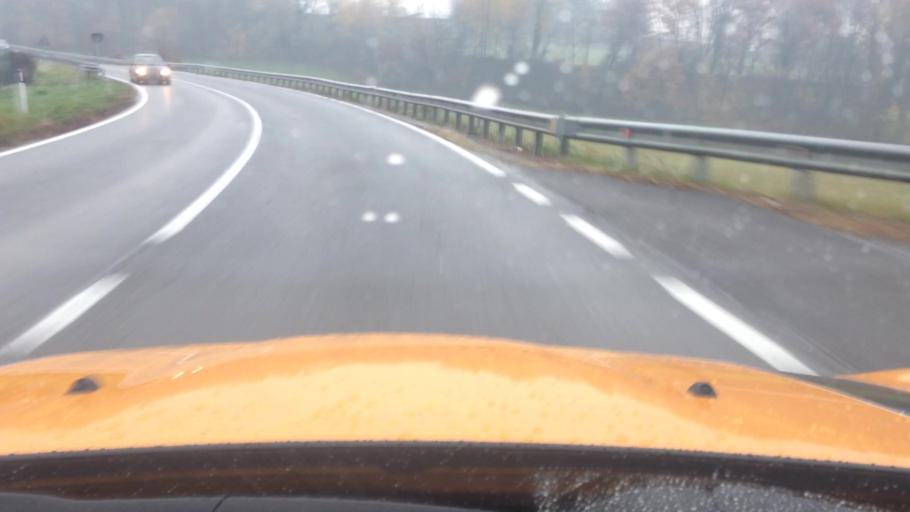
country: IT
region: Lombardy
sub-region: Provincia di Como
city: Senna Comasco
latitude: 45.7552
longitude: 9.1195
